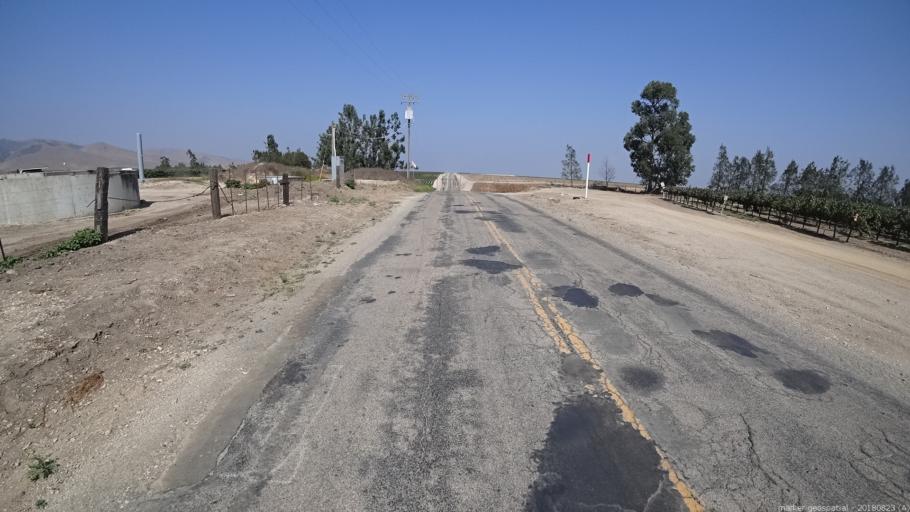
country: US
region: California
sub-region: Monterey County
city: Greenfield
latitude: 36.2574
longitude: -121.2043
